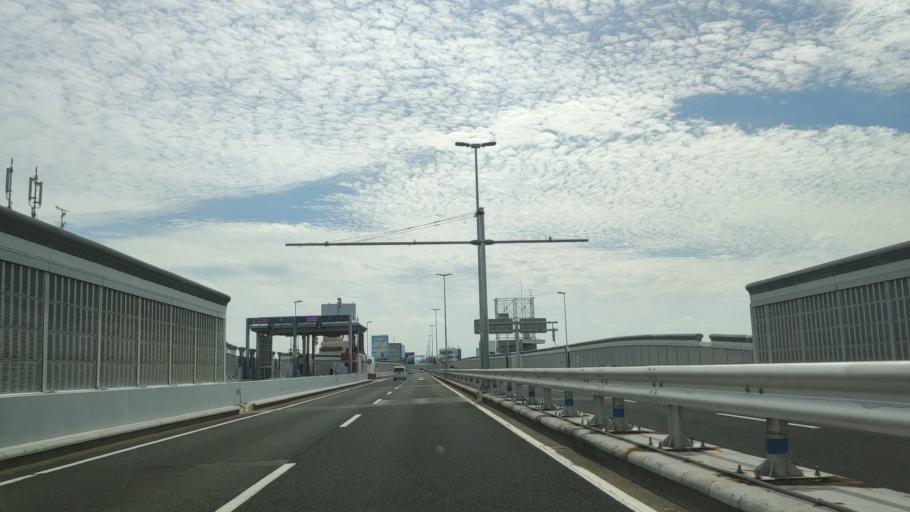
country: JP
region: Osaka
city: Toyonaka
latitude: 34.7805
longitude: 135.4547
